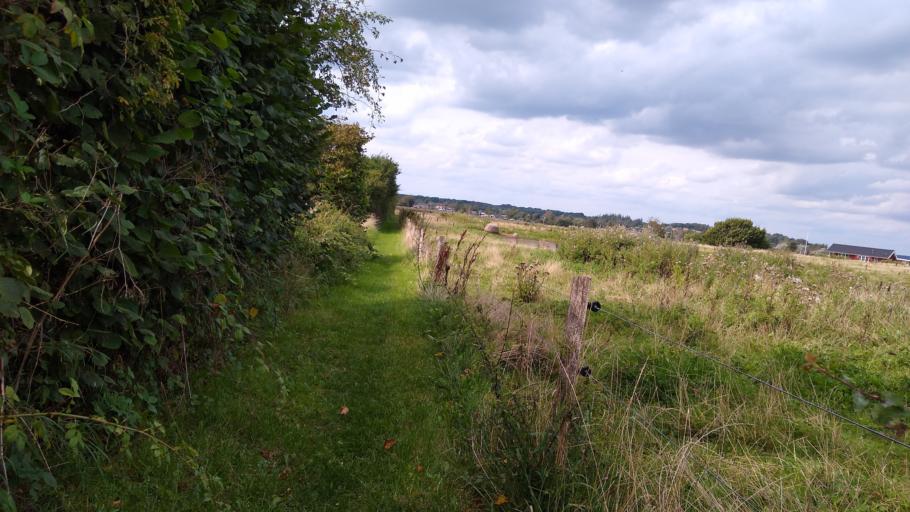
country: DK
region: South Denmark
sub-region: Fredericia Kommune
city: Fredericia
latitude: 55.6236
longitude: 9.7486
